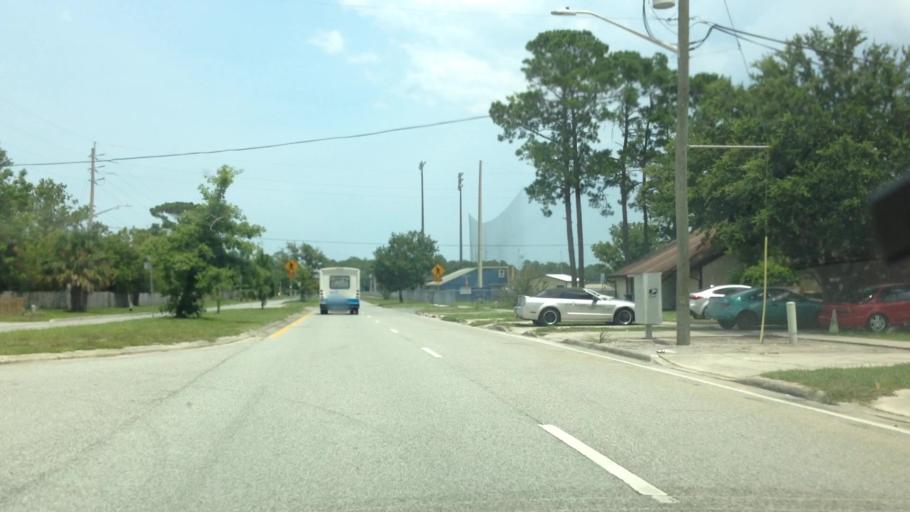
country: US
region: Florida
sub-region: Duval County
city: Neptune Beach
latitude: 30.3012
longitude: -81.5215
